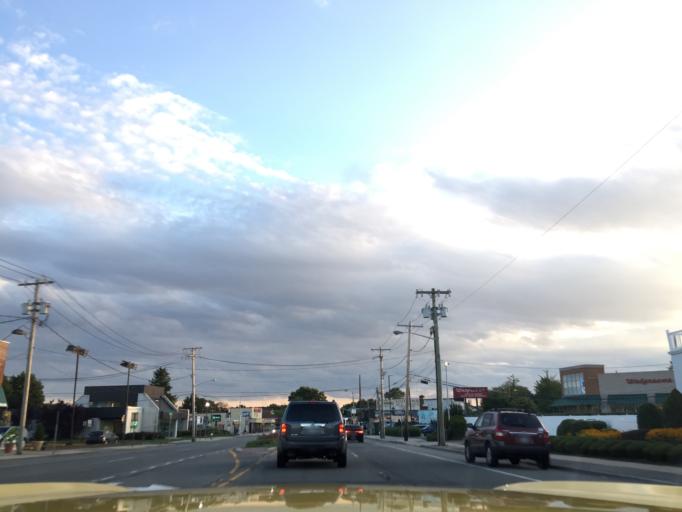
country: US
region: New York
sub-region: Nassau County
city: North New Hyde Park
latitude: 40.7399
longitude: -73.6991
